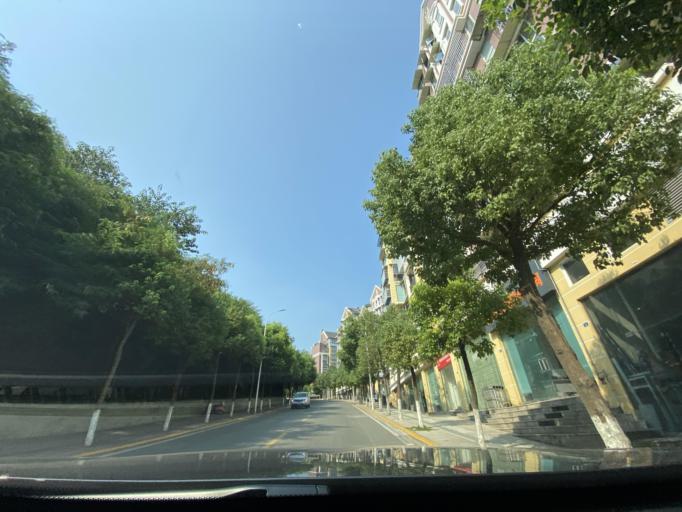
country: CN
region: Sichuan
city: Jiancheng
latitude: 30.4190
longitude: 104.5442
